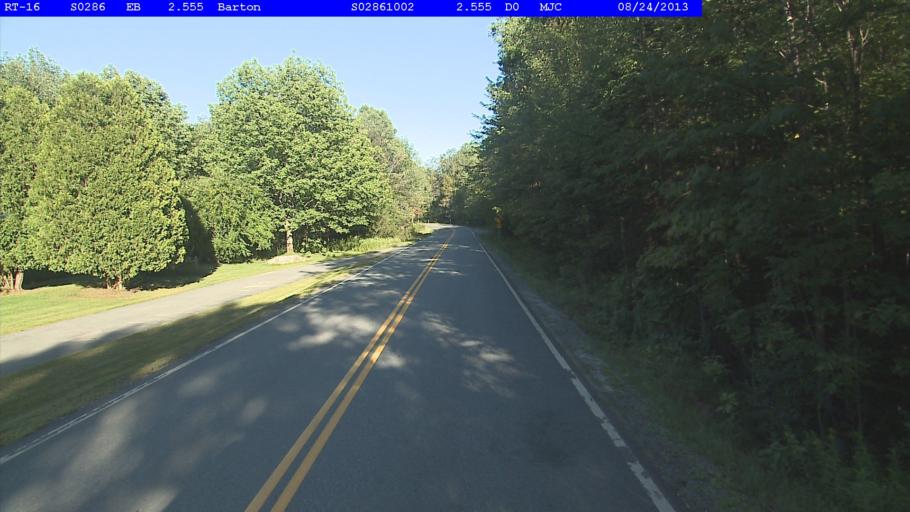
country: US
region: Vermont
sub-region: Orleans County
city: Newport
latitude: 44.7629
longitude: -72.1352
